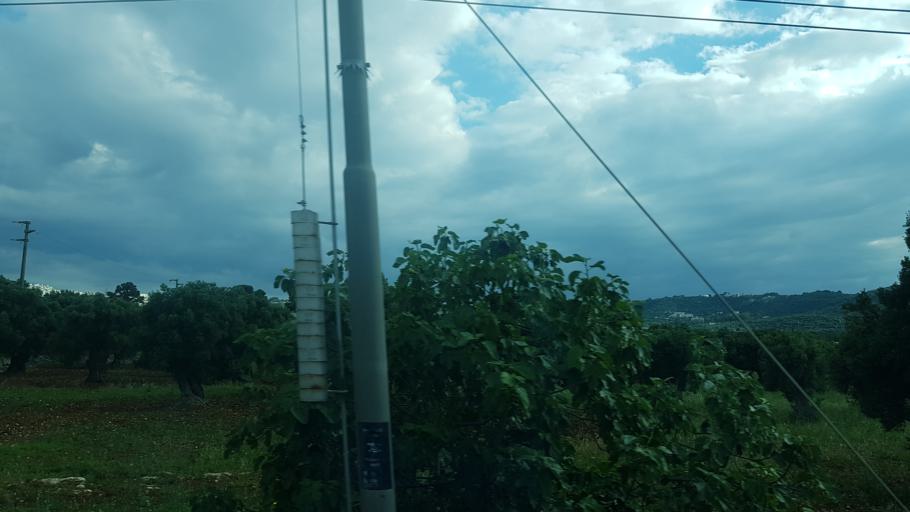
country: IT
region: Apulia
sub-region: Provincia di Brindisi
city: Ostuni
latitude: 40.7545
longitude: 17.5734
